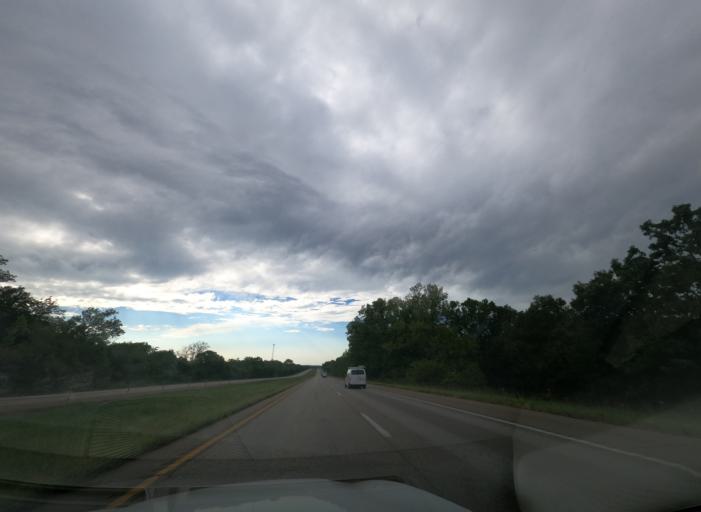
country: US
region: Missouri
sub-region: Sainte Genevieve County
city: Sainte Genevieve
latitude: 37.9592
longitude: -90.1639
